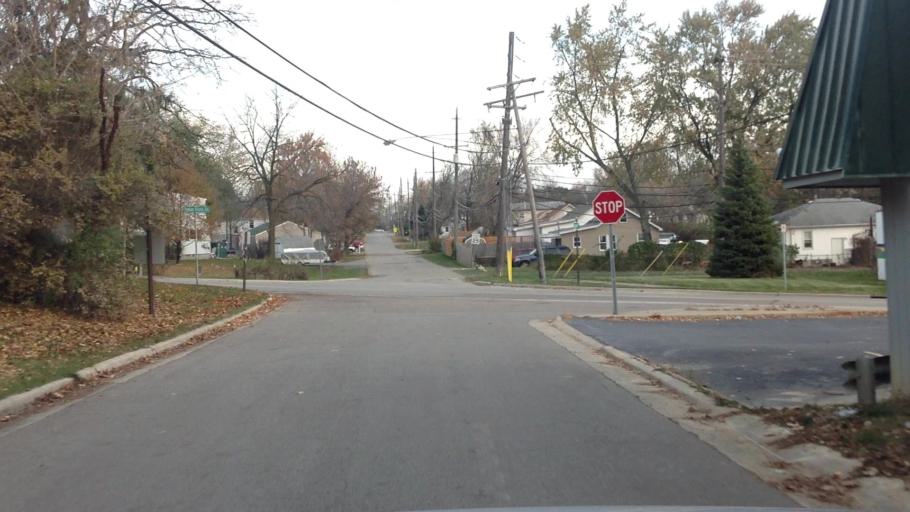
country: US
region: Michigan
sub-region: Oakland County
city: Sylvan Lake
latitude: 42.6302
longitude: -83.3354
